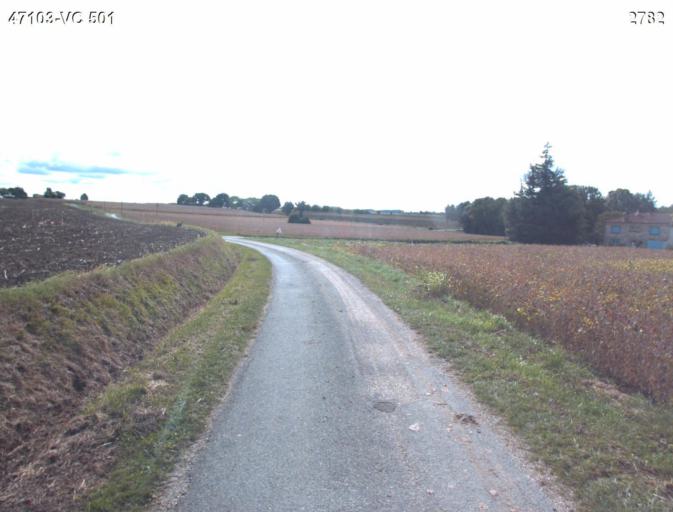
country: FR
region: Aquitaine
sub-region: Departement du Lot-et-Garonne
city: Nerac
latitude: 44.1000
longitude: 0.3219
